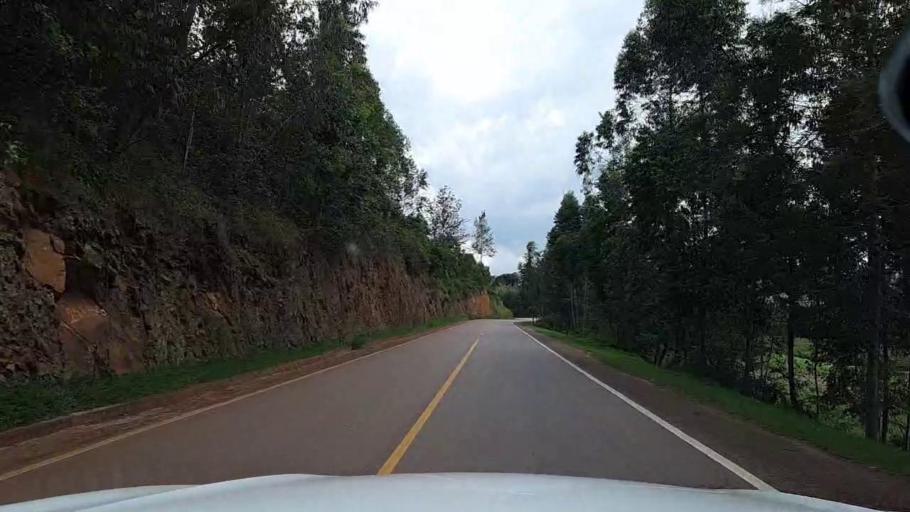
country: RW
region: Kigali
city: Kigali
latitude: -1.8170
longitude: 30.1177
